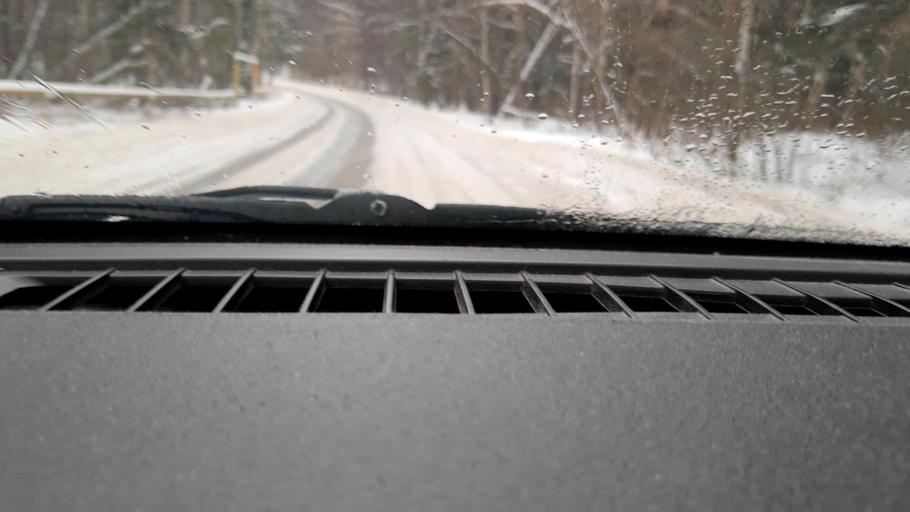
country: RU
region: Nizjnij Novgorod
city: Afonino
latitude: 56.1798
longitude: 44.0795
